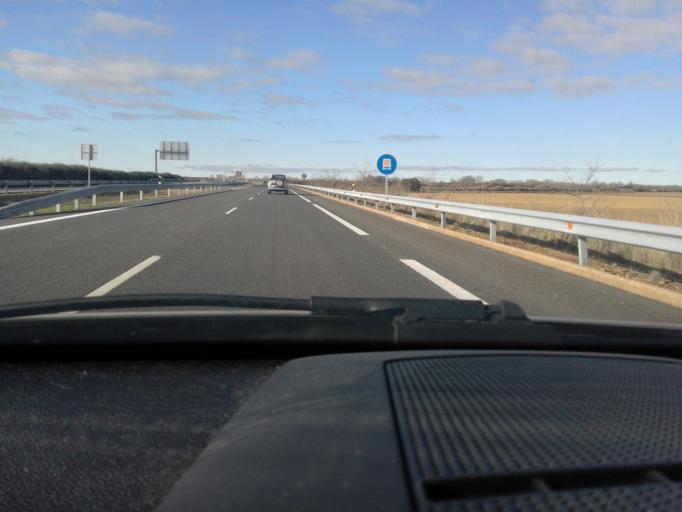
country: ES
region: Castille and Leon
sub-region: Provincia de Palencia
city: Calzada de los Molinos
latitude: 42.3500
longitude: -4.6336
